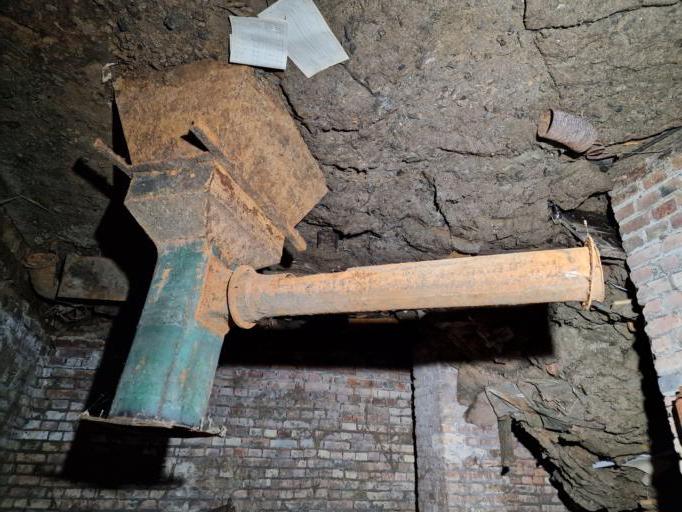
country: PL
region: Lubusz
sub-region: Powiat miedzyrzecki
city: Miedzyrzecz
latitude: 52.4430
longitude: 15.5981
